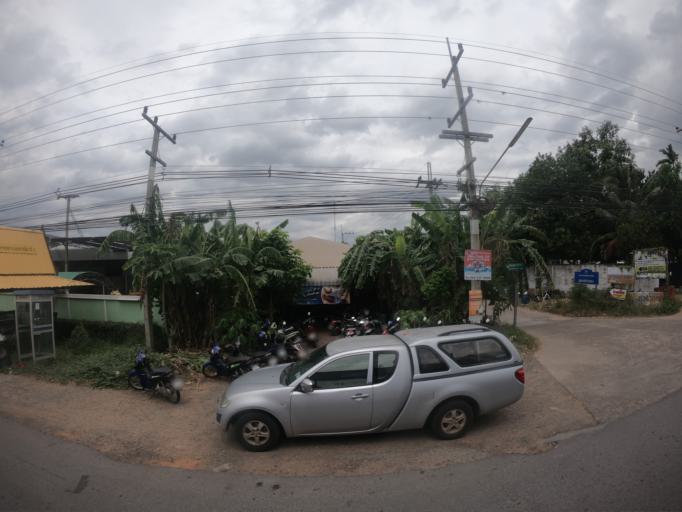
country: TH
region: Nakhon Ratchasima
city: Chok Chai
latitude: 14.8316
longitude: 102.1836
